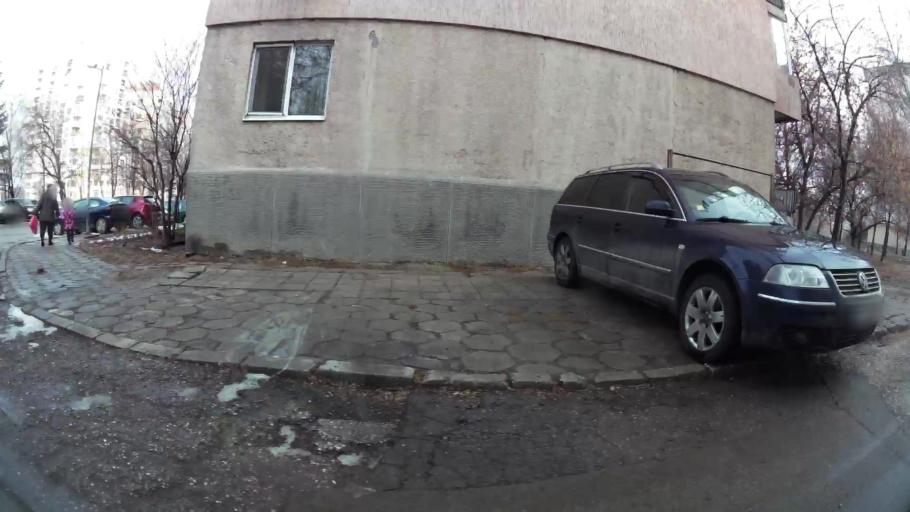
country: BG
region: Sofiya
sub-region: Obshtina Bozhurishte
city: Bozhurishte
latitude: 42.7230
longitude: 23.2430
